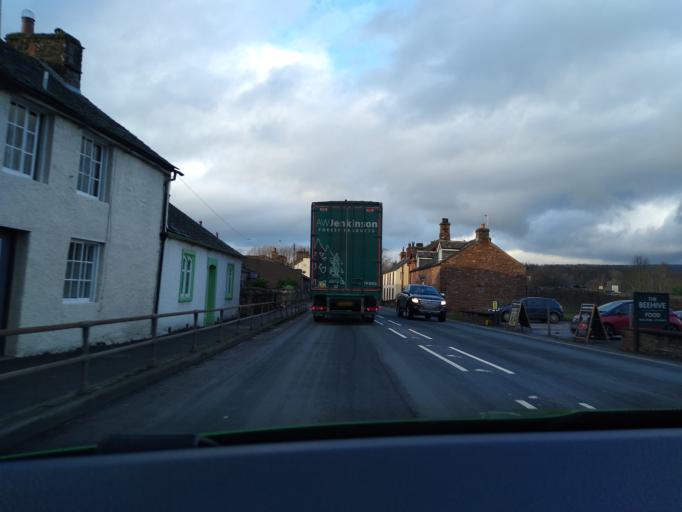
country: GB
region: England
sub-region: Cumbria
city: Penrith
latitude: 54.6491
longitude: -2.7402
